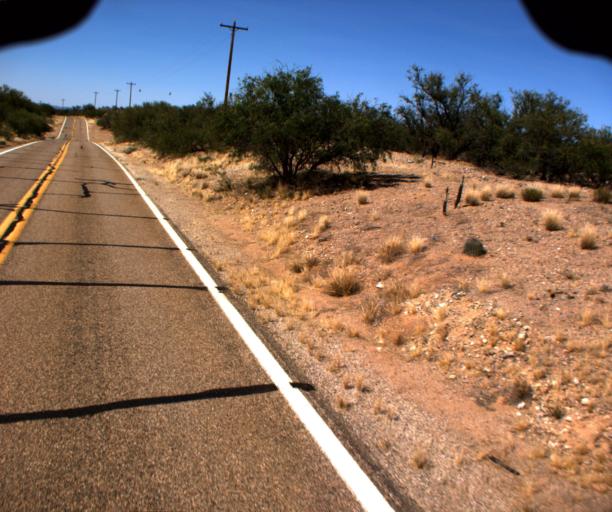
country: US
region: Arizona
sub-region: Pima County
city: Three Points
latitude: 31.8728
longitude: -111.3953
